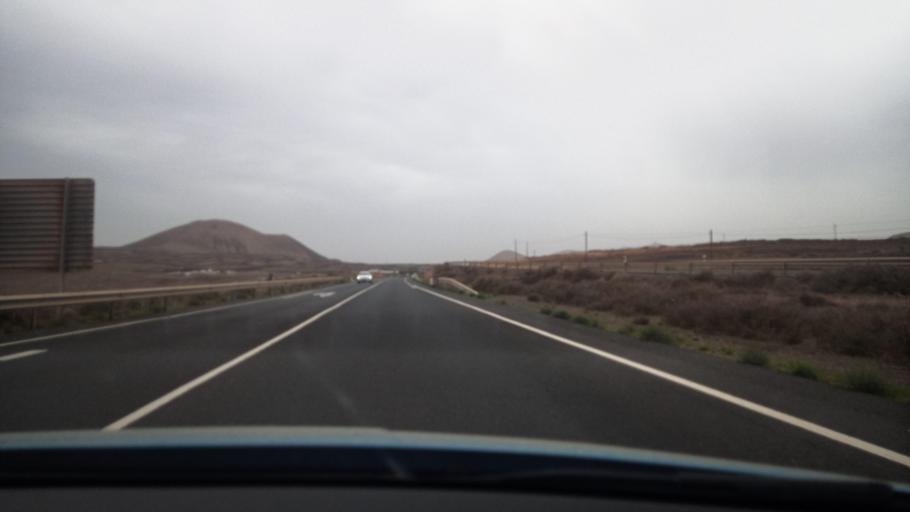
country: ES
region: Canary Islands
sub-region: Provincia de Las Palmas
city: Nazaret
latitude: 29.0289
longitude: -13.5250
